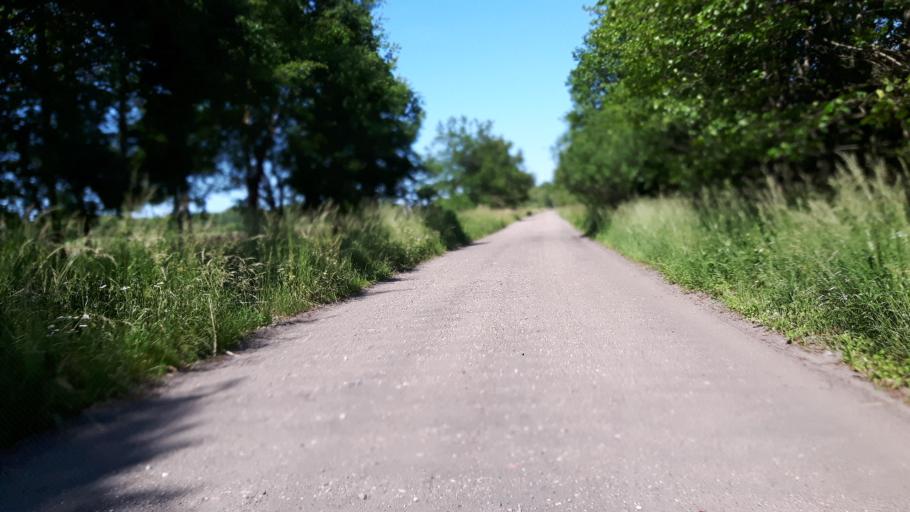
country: PL
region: Pomeranian Voivodeship
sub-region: Powiat slupski
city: Glowczyce
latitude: 54.6884
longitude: 17.4434
